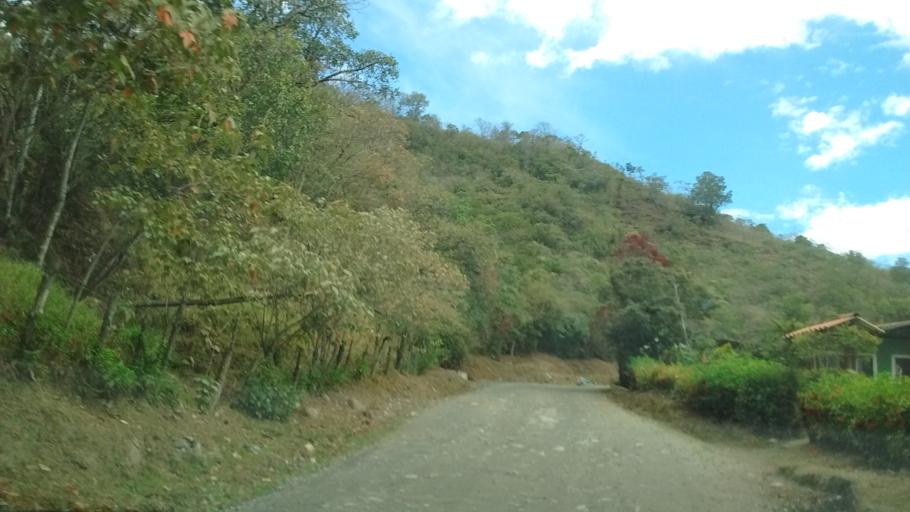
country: CO
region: Cauca
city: Almaguer
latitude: 1.8519
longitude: -76.9278
